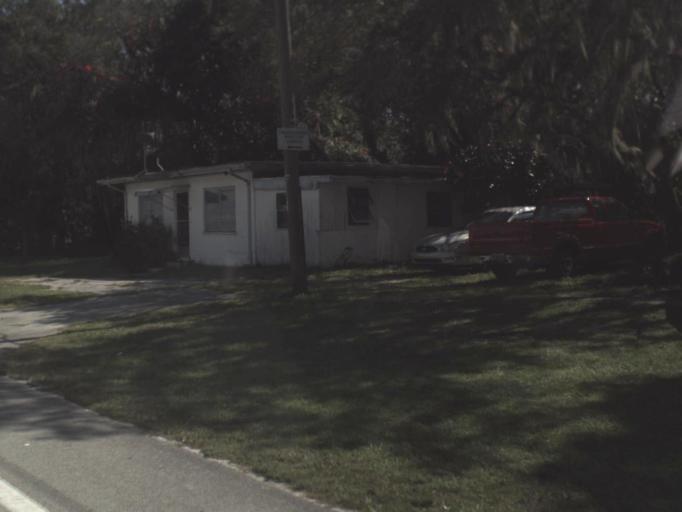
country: US
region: Florida
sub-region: Highlands County
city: Sebring
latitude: 27.4284
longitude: -81.4133
